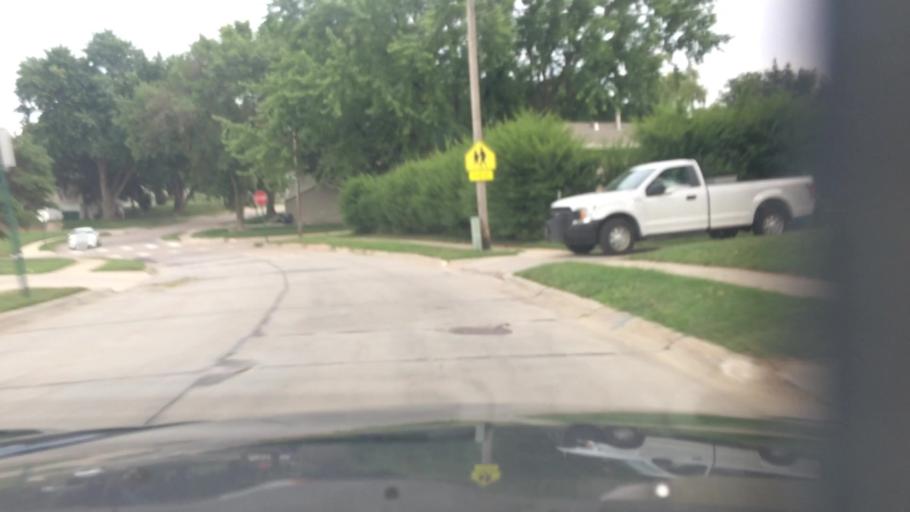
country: US
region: Nebraska
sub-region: Sarpy County
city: La Vista
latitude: 41.1847
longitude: -96.0519
